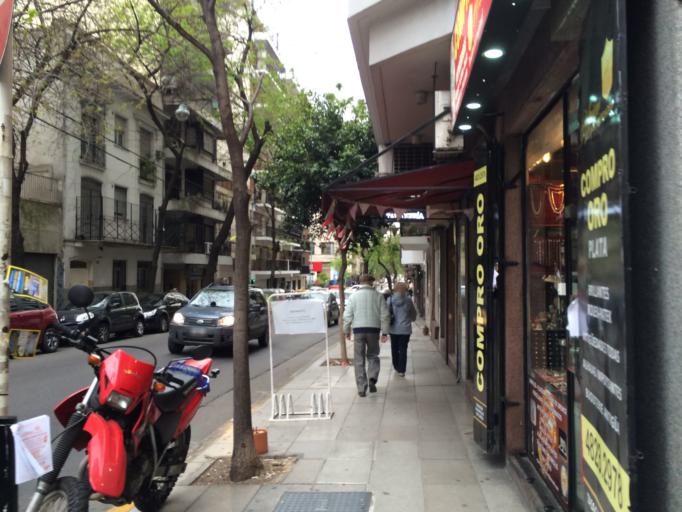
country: AR
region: Buenos Aires F.D.
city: Retiro
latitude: -34.5909
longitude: -58.4063
